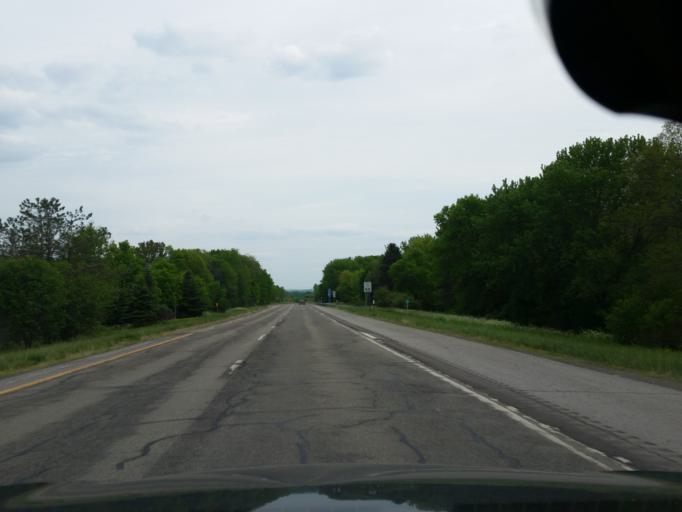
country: US
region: New York
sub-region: Chautauqua County
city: Lakewood
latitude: 42.1635
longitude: -79.3824
